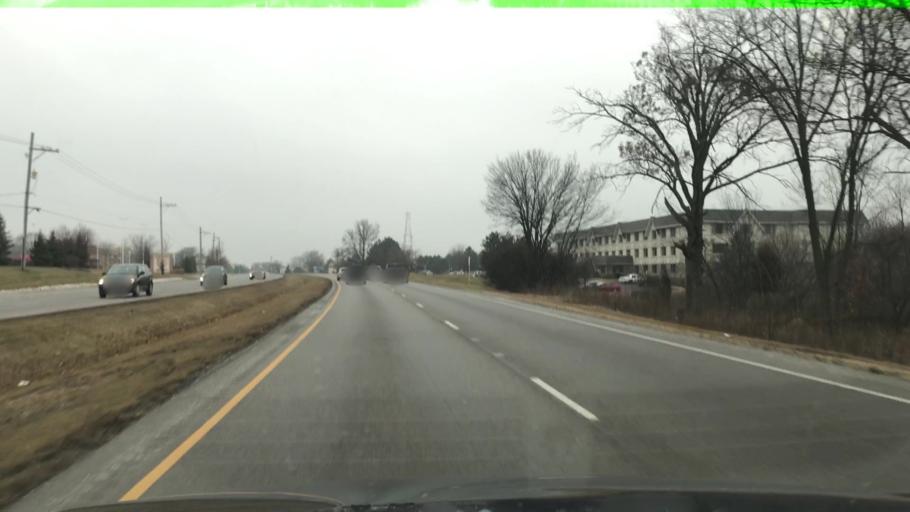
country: US
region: Illinois
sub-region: Lake County
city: Lake Zurich
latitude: 42.1812
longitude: -88.0809
